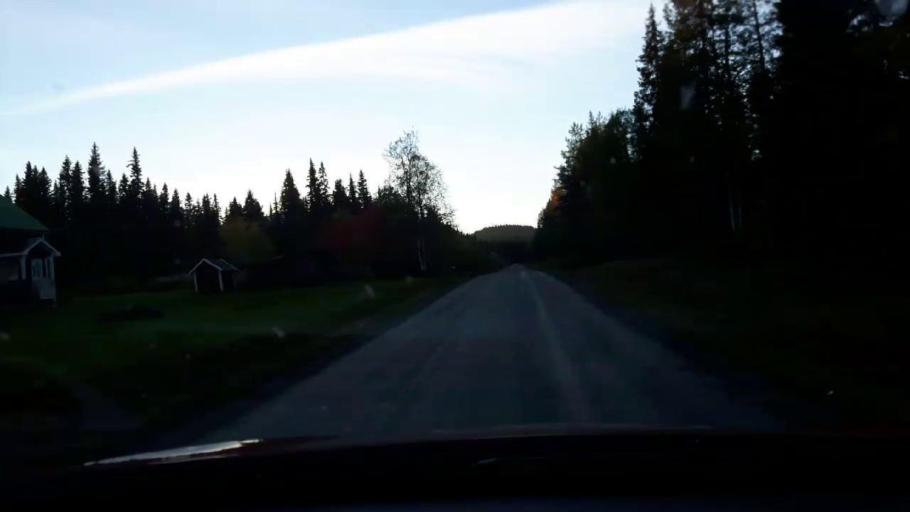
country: SE
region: Jaemtland
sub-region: Krokoms Kommun
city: Krokom
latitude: 63.4788
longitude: 14.2248
